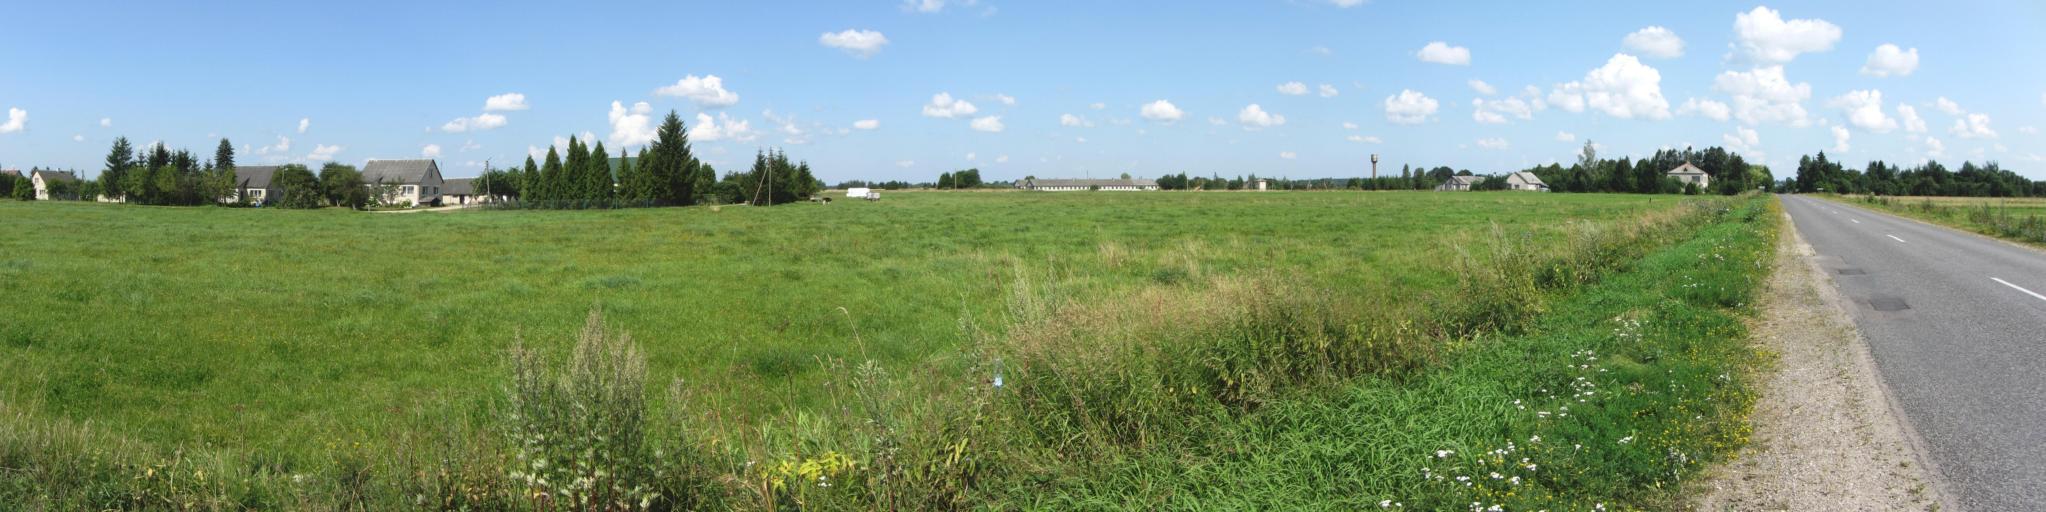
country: LT
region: Vilnius County
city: Ukmerge
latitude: 55.0347
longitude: 24.6765
